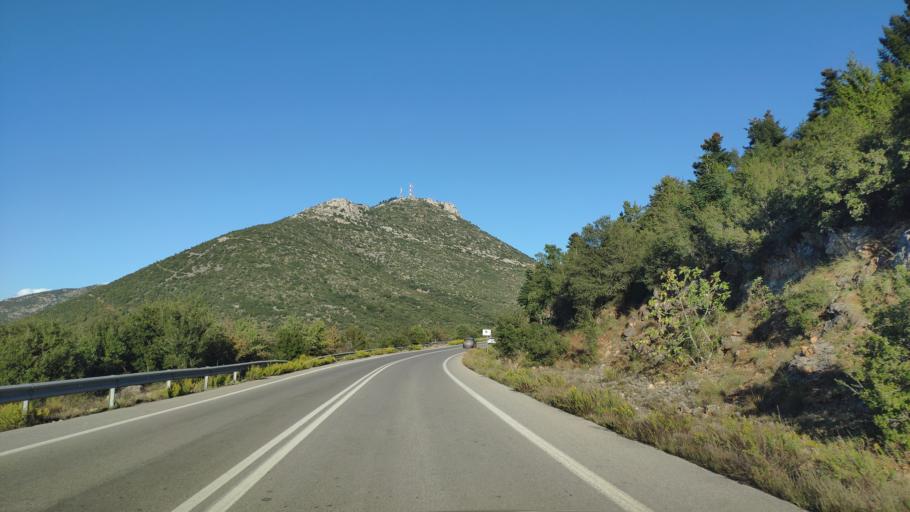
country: GR
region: Peloponnese
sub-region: Nomos Arkadias
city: Langadhia
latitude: 37.7258
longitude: 22.2225
